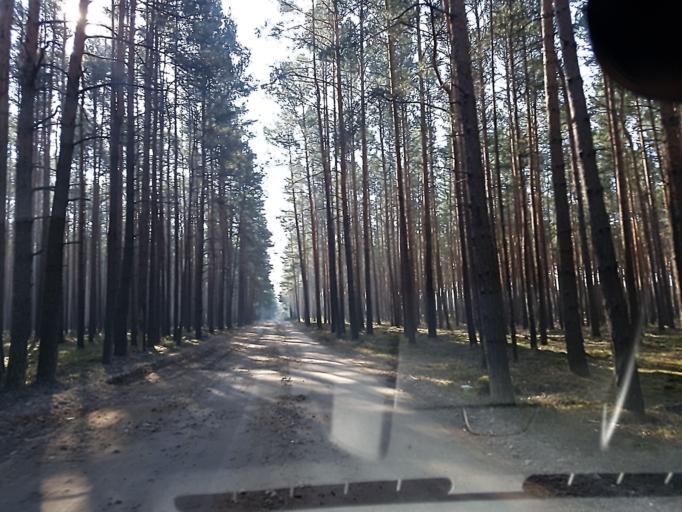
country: DE
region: Brandenburg
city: Tschernitz
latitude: 51.6600
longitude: 14.5650
